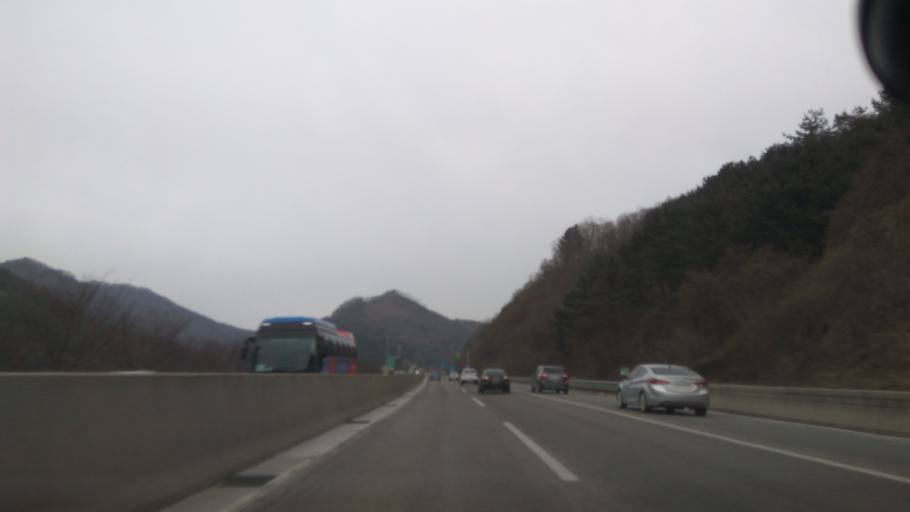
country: KR
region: Gyeonggi-do
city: Cheongpyeong
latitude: 37.6455
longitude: 127.4197
